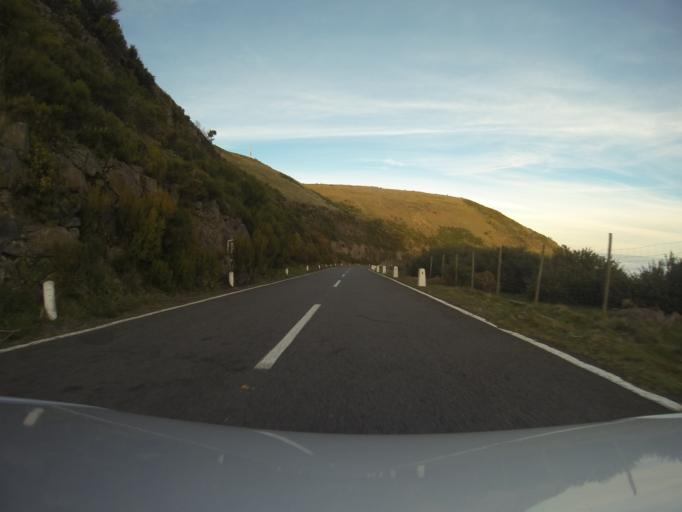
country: PT
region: Madeira
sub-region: Sao Vicente
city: Sao Vicente
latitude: 32.7336
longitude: -17.0580
